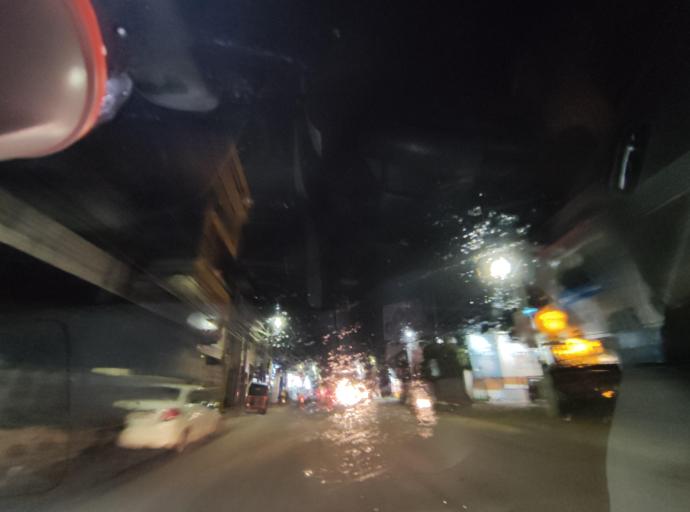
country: IN
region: Kerala
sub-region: Thiruvananthapuram
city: Thiruvananthapuram
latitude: 8.4767
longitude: 76.9480
